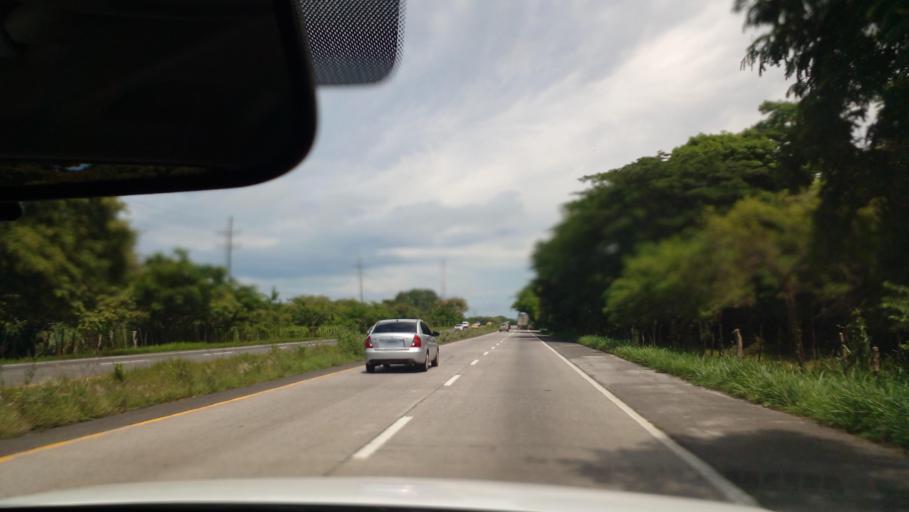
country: PA
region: Panama
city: Nueva Gorgona
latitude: 8.4846
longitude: -79.9582
